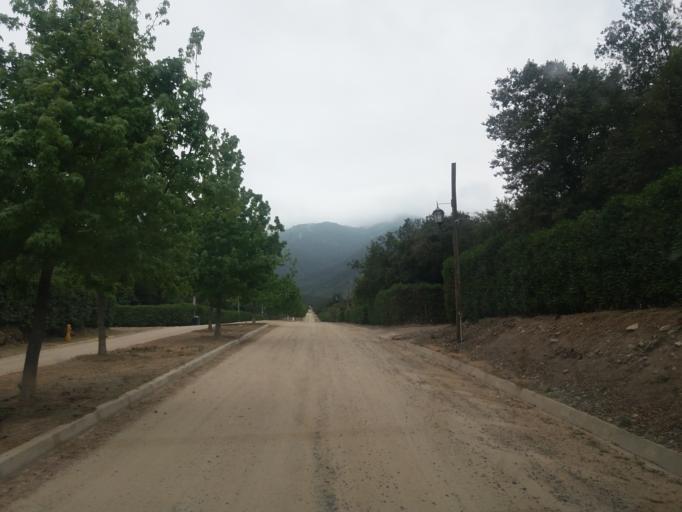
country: CL
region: Valparaiso
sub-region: Provincia de Marga Marga
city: Limache
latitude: -33.0282
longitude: -71.1364
